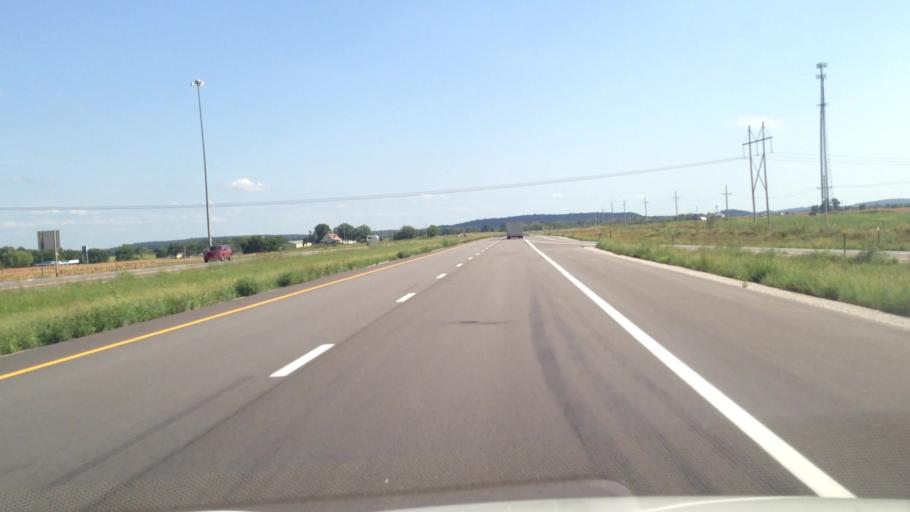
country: US
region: Kansas
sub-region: Linn County
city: La Cygne
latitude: 38.3436
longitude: -94.6822
